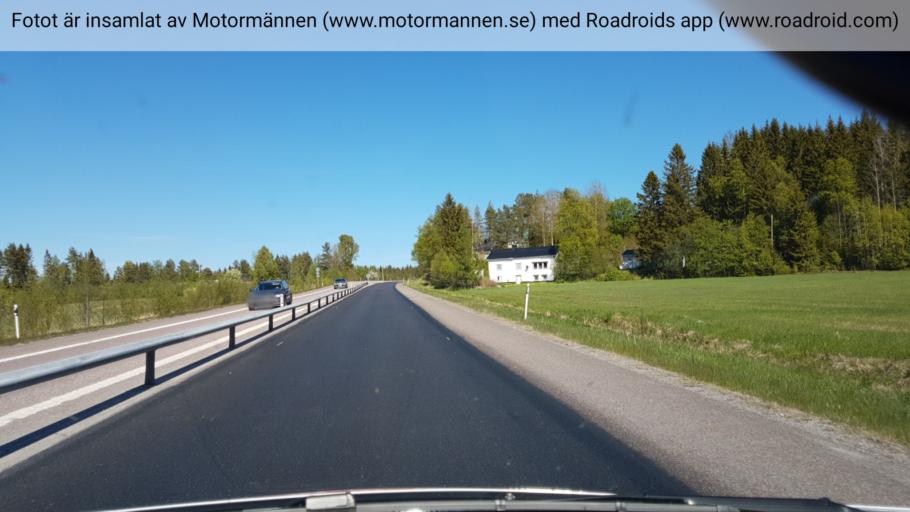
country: SE
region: Vaesternorrland
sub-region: OErnskoeldsviks Kommun
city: Husum
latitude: 63.3330
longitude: 19.0624
